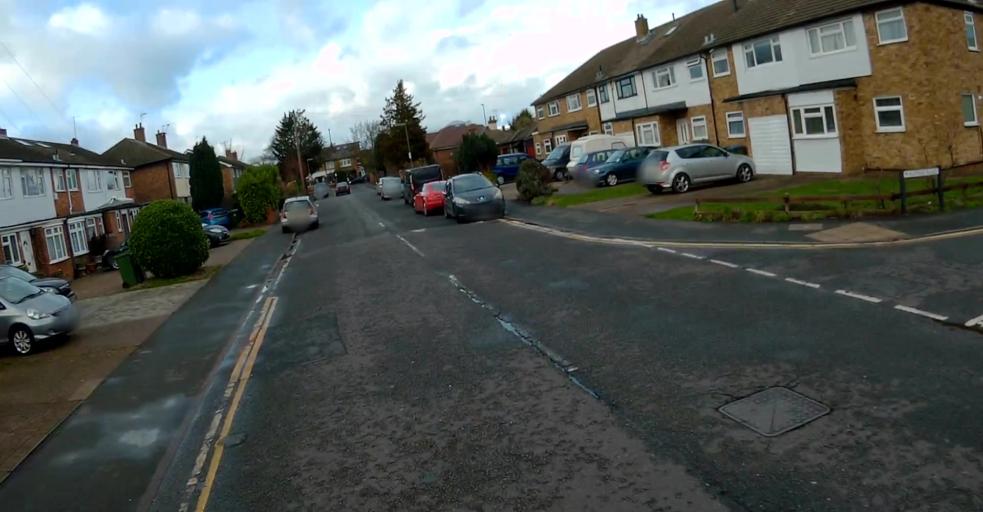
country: GB
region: England
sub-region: Surrey
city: Walton-on-Thames
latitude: 51.3883
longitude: -0.4148
